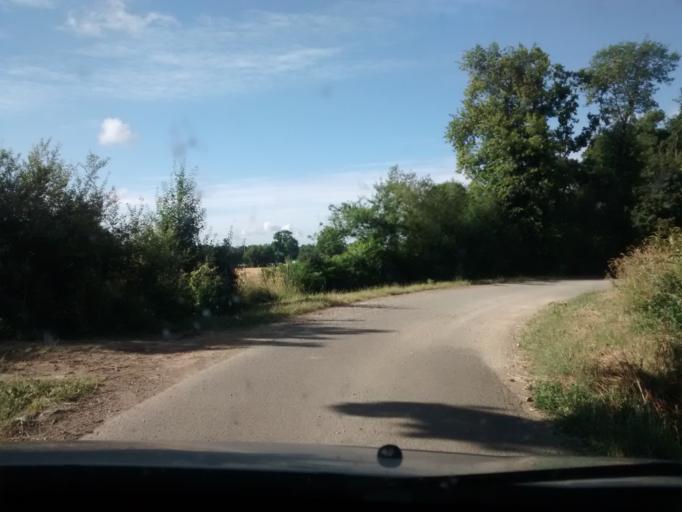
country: FR
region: Brittany
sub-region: Departement d'Ille-et-Vilaine
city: Plechatel
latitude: 47.8430
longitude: -1.7418
